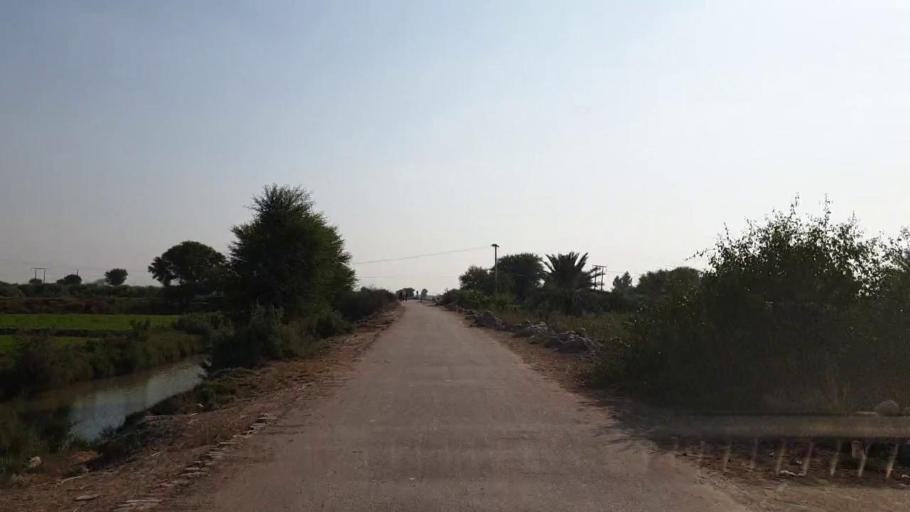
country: PK
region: Sindh
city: Sehwan
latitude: 26.4474
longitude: 67.8144
